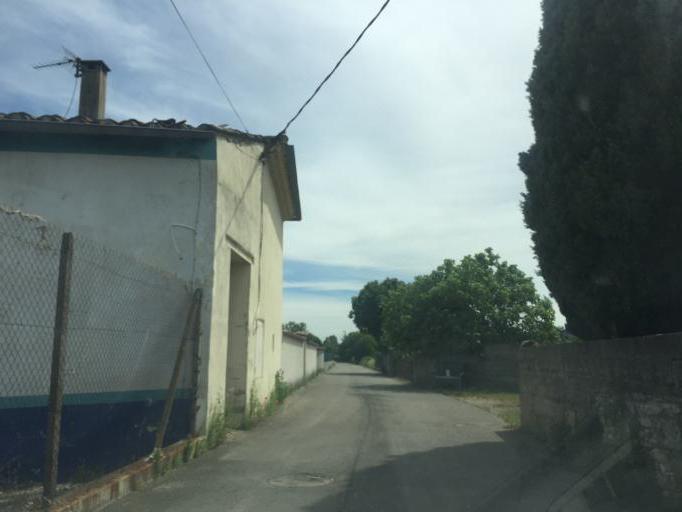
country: FR
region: Rhone-Alpes
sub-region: Departement de l'Ardeche
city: Bourg-Saint-Andeol
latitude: 44.3640
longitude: 4.6463
